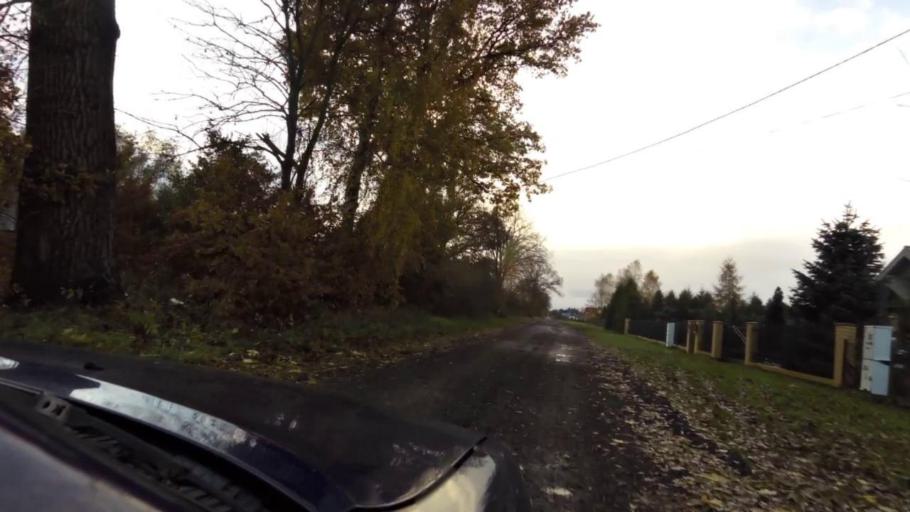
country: PL
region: West Pomeranian Voivodeship
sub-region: Powiat goleniowski
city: Goleniow
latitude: 53.5876
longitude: 14.7614
